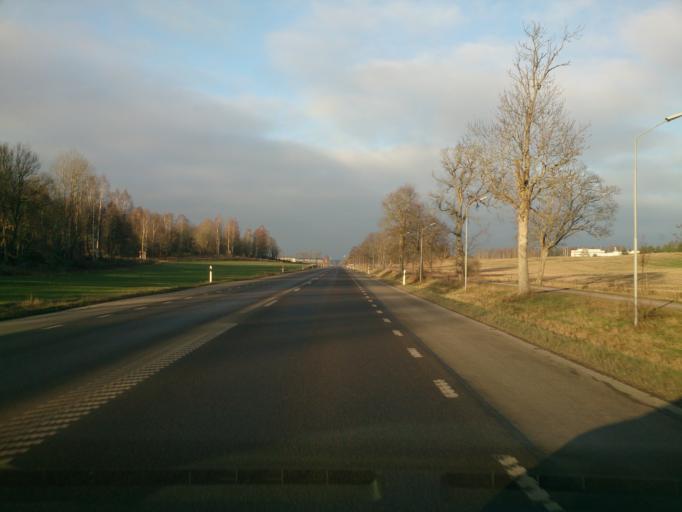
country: SE
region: OEstergoetland
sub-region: Atvidabergs Kommun
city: Atvidaberg
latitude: 58.2204
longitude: 15.9724
